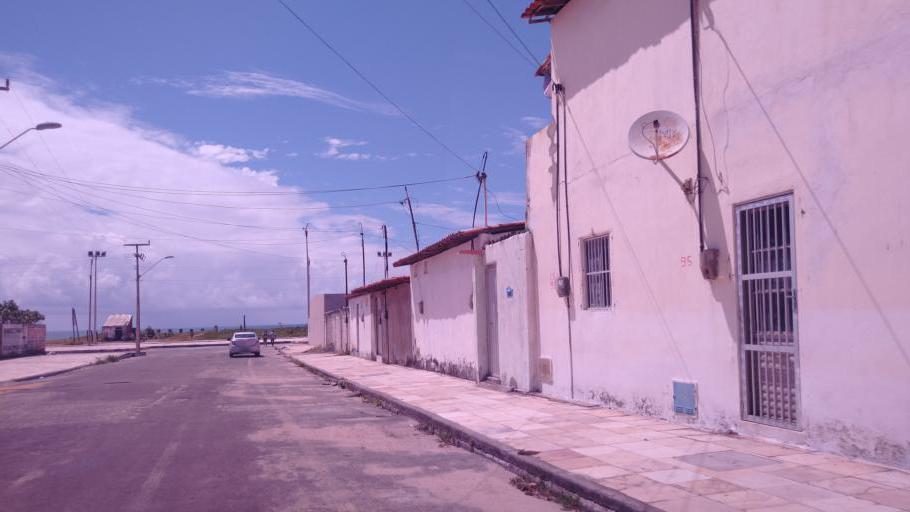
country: BR
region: Ceara
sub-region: Fortaleza
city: Fortaleza
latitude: -3.7263
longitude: -38.4612
